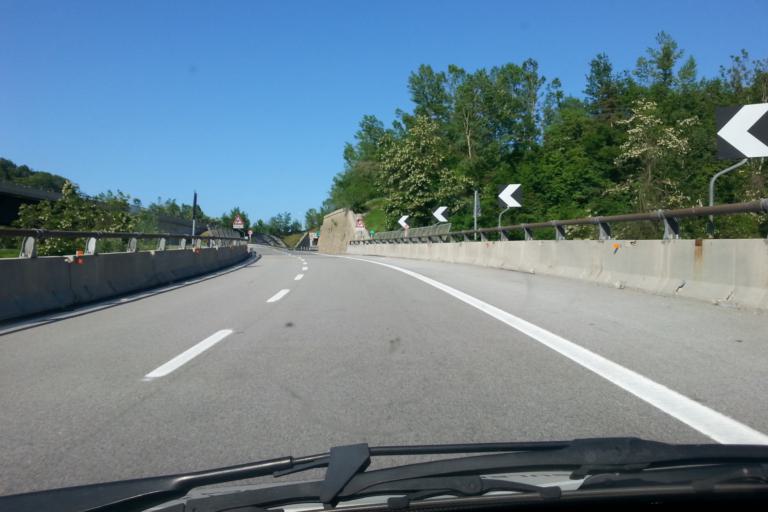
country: IT
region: Liguria
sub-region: Provincia di Savona
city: Cosseria
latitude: 44.3565
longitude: 8.2241
